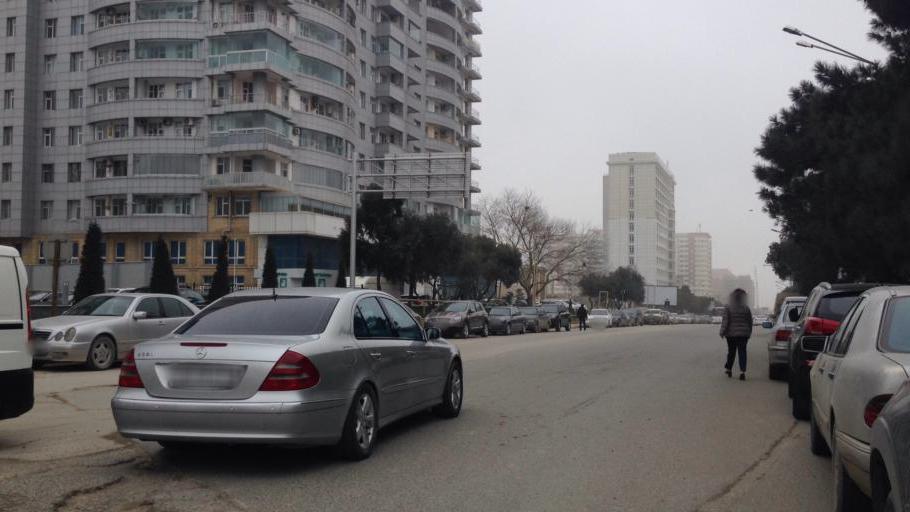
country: AZ
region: Baki
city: Baku
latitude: 40.3884
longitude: 49.8757
